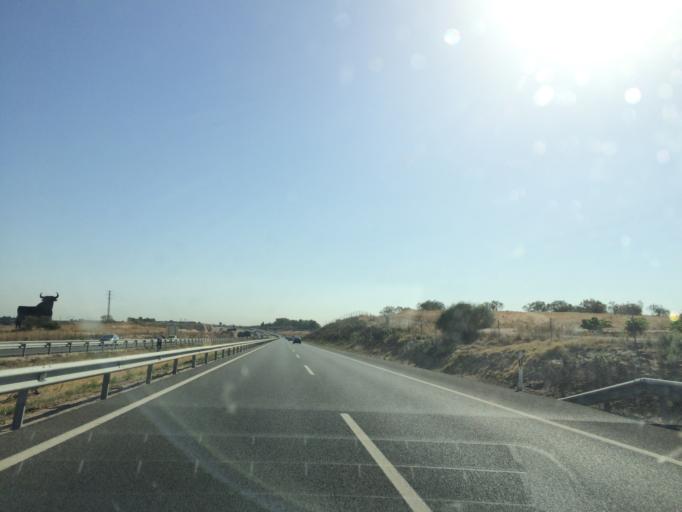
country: ES
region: Castille-La Mancha
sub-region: Province of Toledo
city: Valmojado
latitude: 40.2153
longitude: -4.0903
